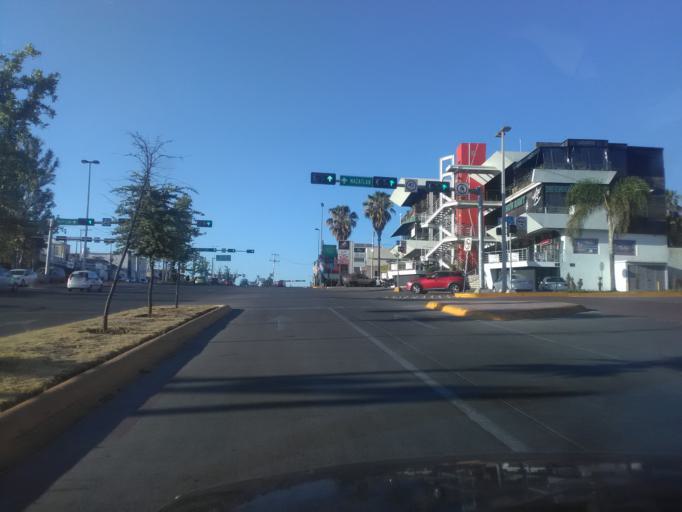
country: MX
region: Durango
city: Victoria de Durango
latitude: 24.0208
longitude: -104.6903
